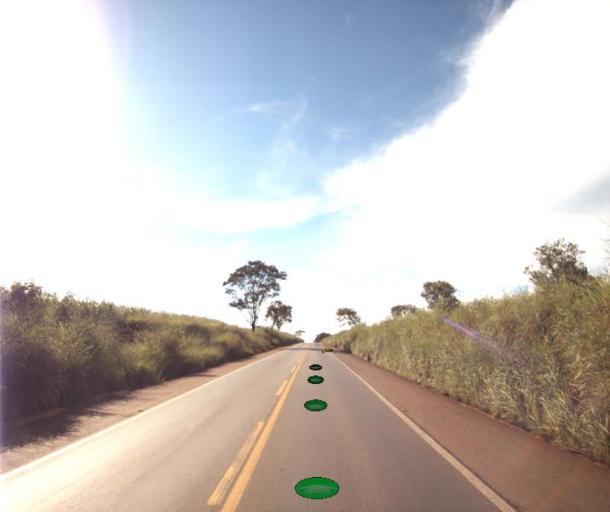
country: BR
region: Goias
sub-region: Rialma
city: Rialma
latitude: -15.3660
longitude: -49.5609
